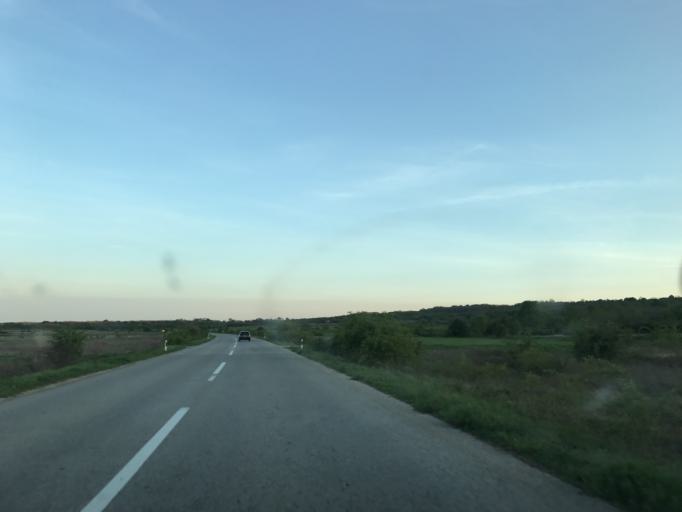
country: RO
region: Mehedinti
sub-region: Comuna Gogosu
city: Ostrovu Mare
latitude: 44.3366
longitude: 22.4739
